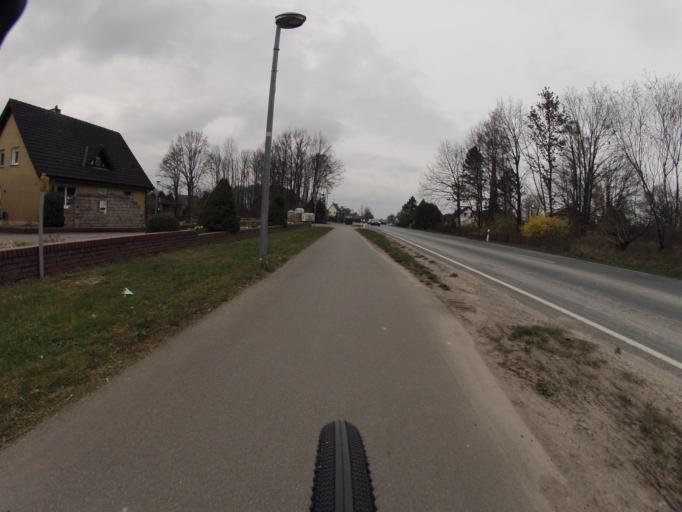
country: DE
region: North Rhine-Westphalia
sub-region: Regierungsbezirk Munster
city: Mettingen
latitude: 52.3376
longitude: 7.7409
